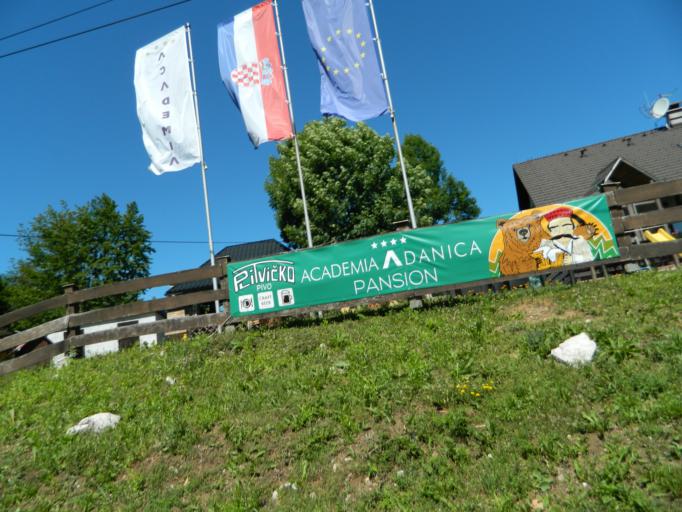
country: HR
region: Licko-Senjska
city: Jezerce
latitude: 44.9101
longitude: 15.6127
